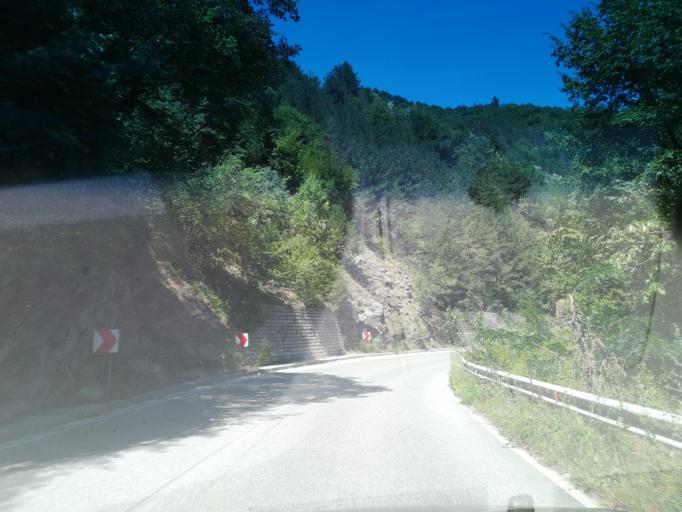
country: BG
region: Plovdiv
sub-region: Obshtina Luki
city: Luki
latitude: 41.9188
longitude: 24.8175
